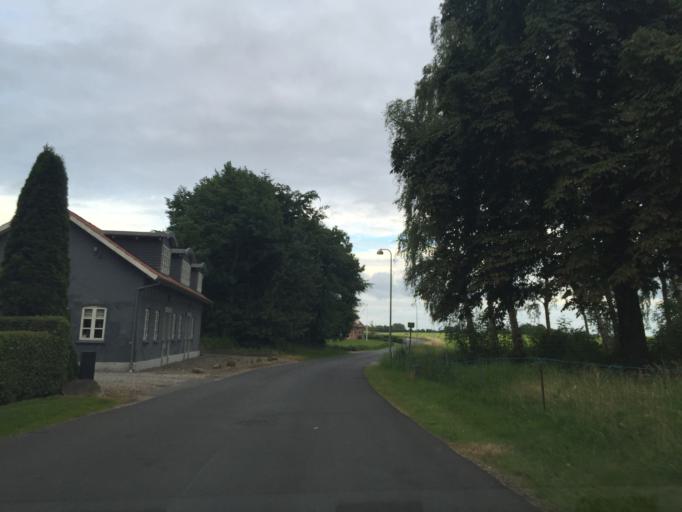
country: DK
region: Central Jutland
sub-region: Silkeborg Kommune
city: Kjellerup
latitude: 56.2445
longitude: 9.4922
